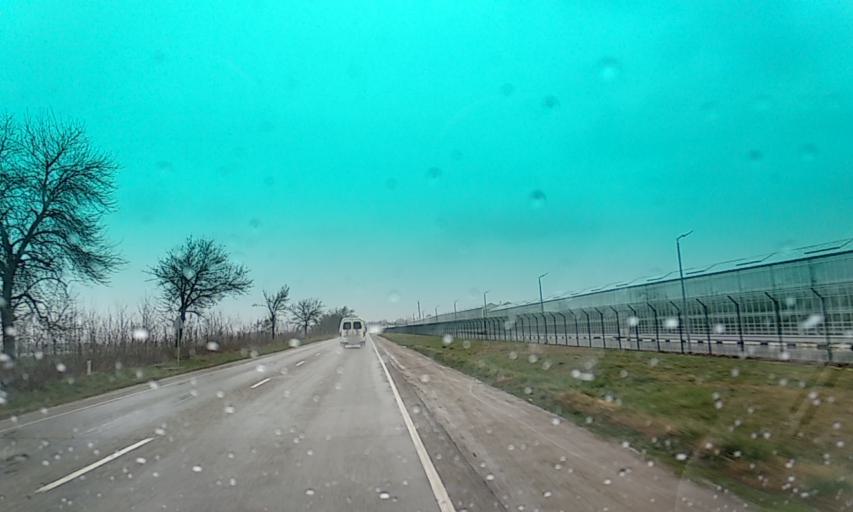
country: RU
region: Krasnodarskiy
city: Belorechensk
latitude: 44.8008
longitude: 39.8588
